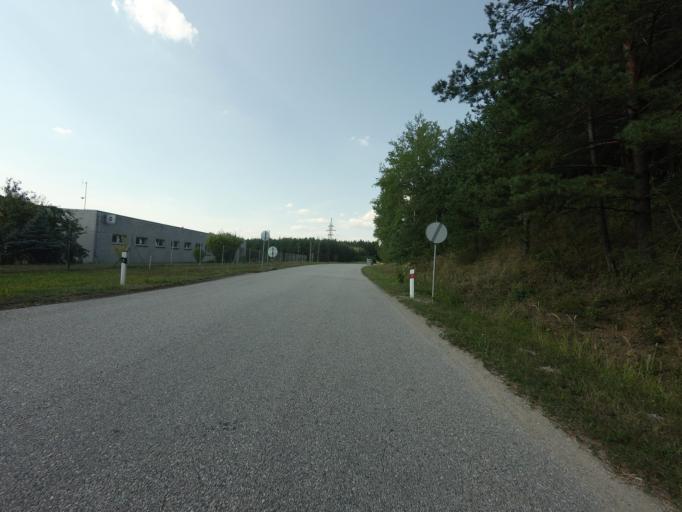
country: CZ
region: Jihocesky
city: Tyn nad Vltavou
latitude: 49.1833
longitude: 14.4472
